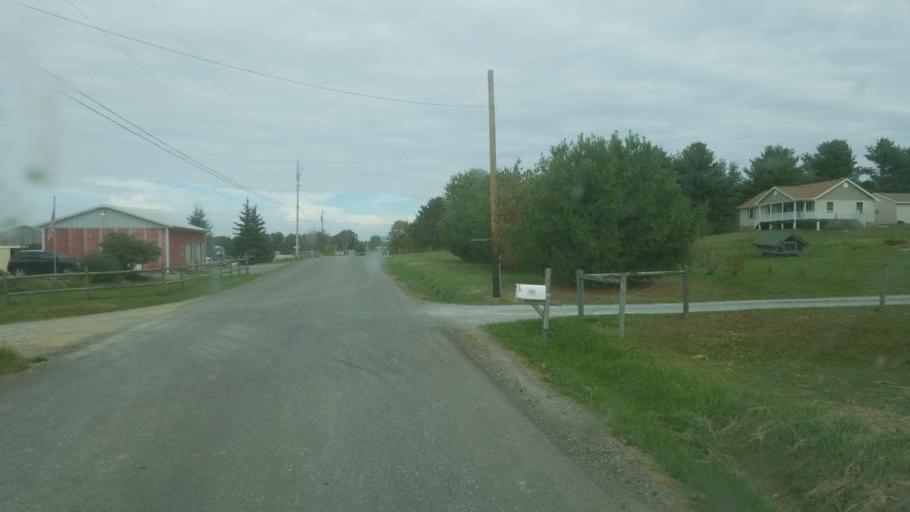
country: US
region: Pennsylvania
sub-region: Mercer County
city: Stoneboro
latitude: 41.3827
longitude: -80.2439
